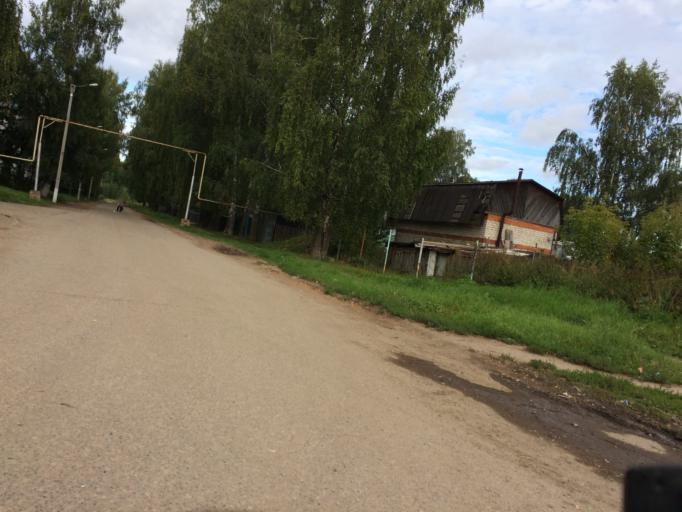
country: RU
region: Mariy-El
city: Yoshkar-Ola
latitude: 56.6562
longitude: 47.9809
